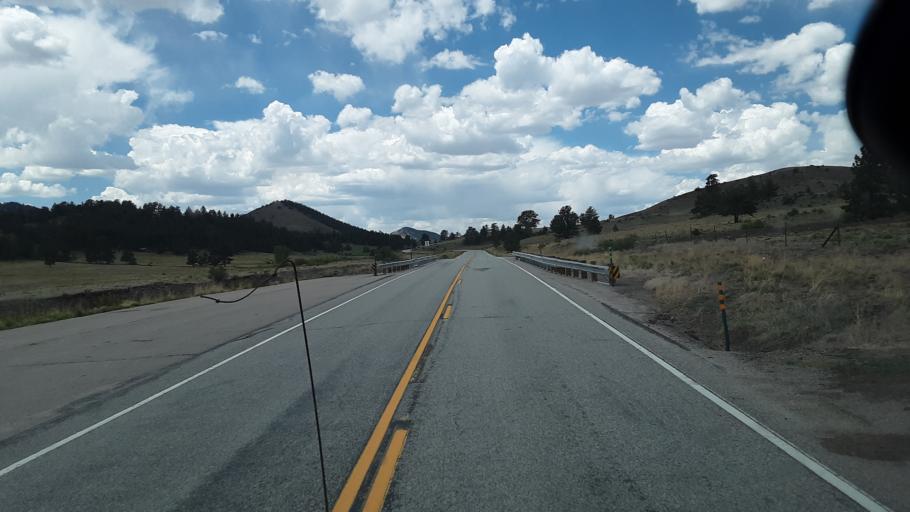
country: US
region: Colorado
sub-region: Teller County
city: Cripple Creek
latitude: 38.7919
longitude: -105.5900
